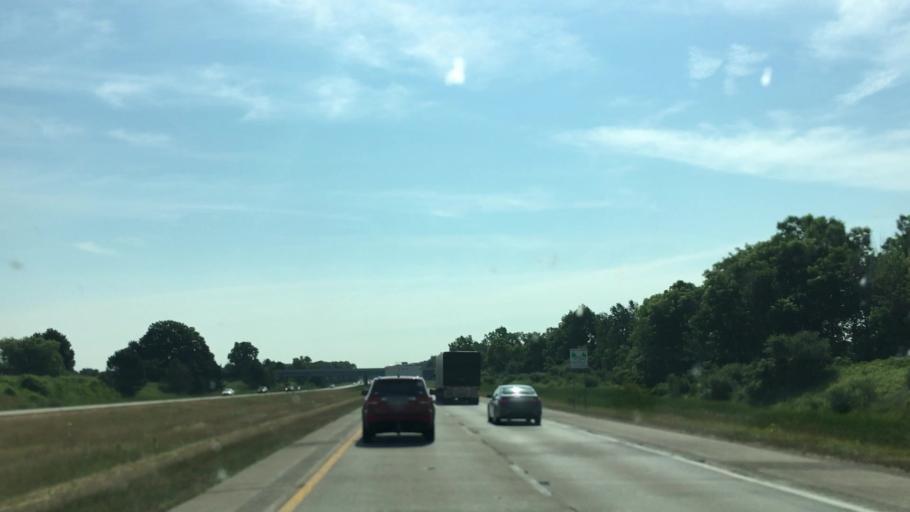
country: US
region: Michigan
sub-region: Clinton County
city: DeWitt
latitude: 42.8074
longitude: -84.6072
